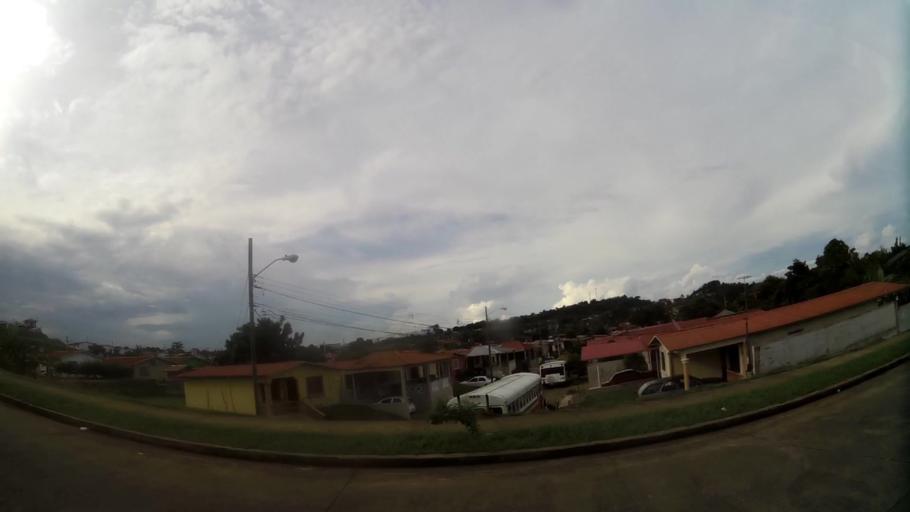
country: PA
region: Panama
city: La Chorrera
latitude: 8.8797
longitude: -79.7647
